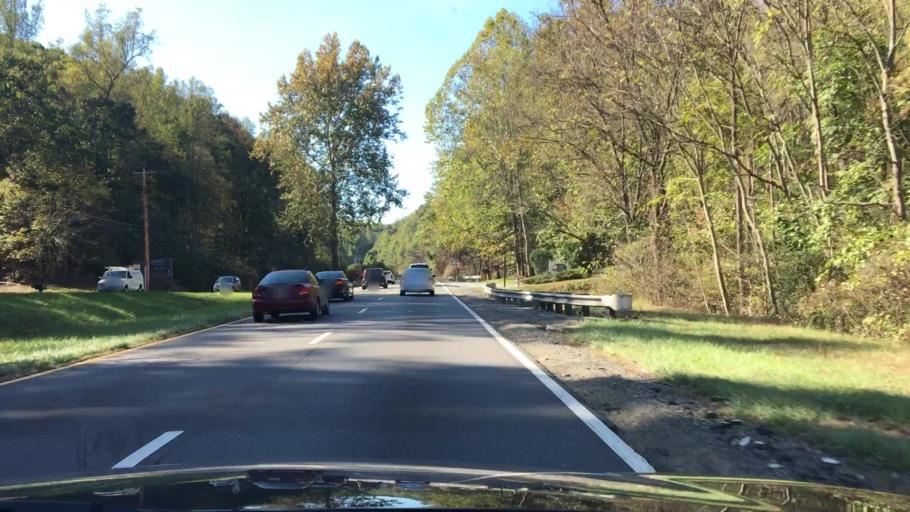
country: US
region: Virginia
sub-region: Roanoke County
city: Narrows
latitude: 37.1566
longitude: -79.9537
